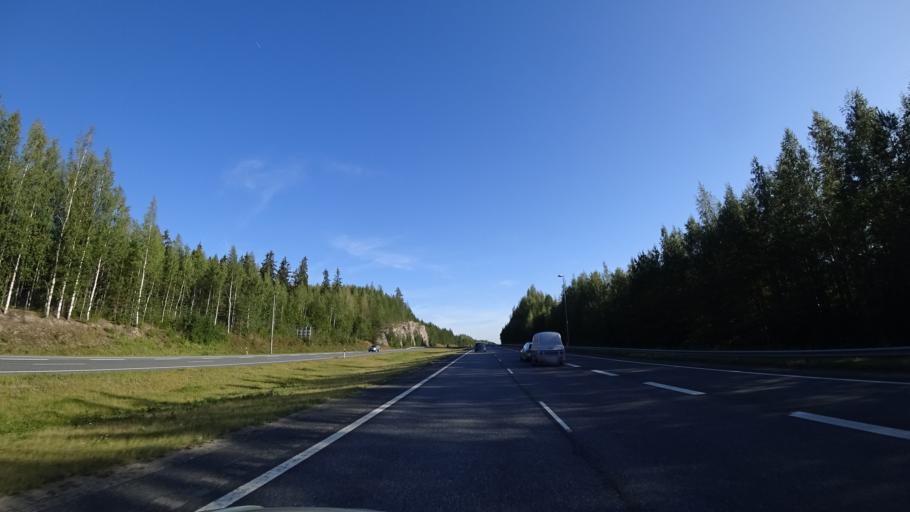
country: FI
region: Haeme
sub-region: Haemeenlinna
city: Tervakoski
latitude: 60.8202
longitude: 24.6701
